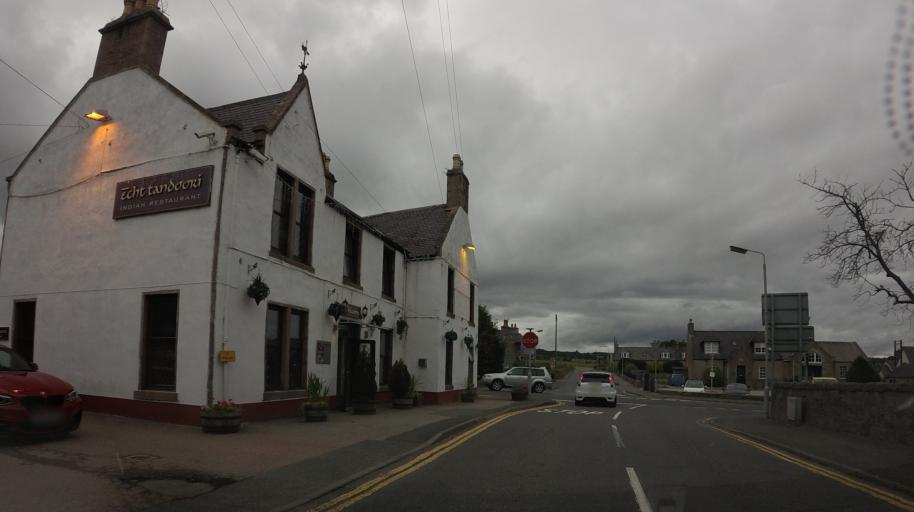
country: GB
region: Scotland
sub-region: Aberdeenshire
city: Kemnay
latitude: 57.1411
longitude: -2.4332
